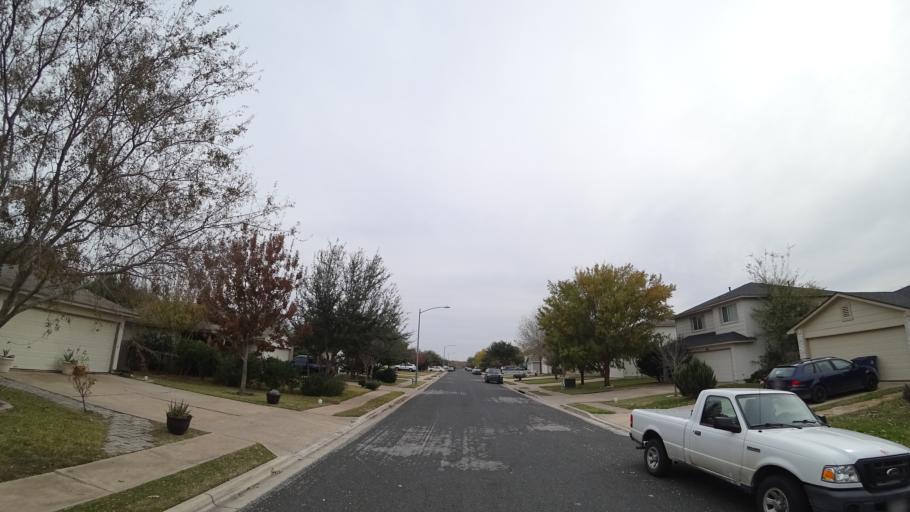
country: US
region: Texas
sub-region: Travis County
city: Onion Creek
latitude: 30.1538
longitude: -97.7408
